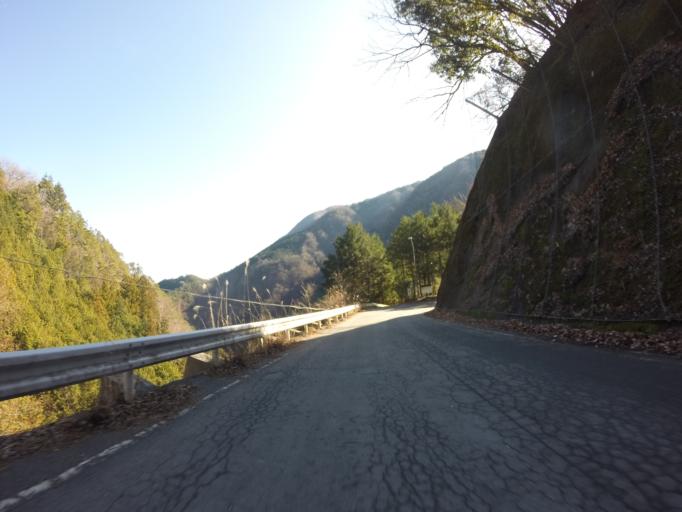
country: JP
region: Yamanashi
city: Ryuo
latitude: 35.4113
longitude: 138.3354
